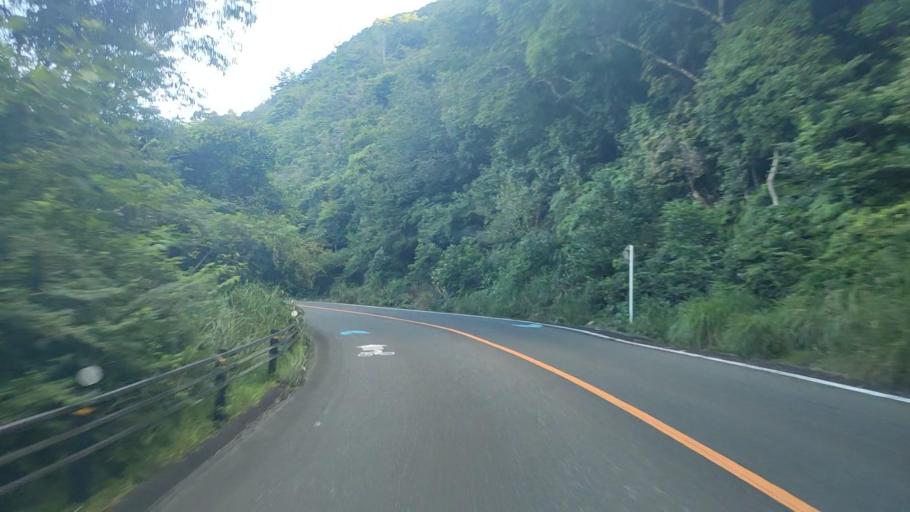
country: JP
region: Mie
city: Toba
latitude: 34.3844
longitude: 136.8606
